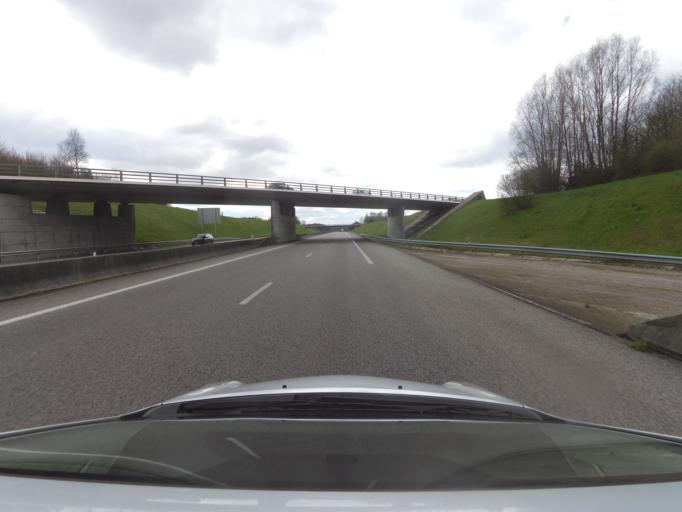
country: FR
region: Haute-Normandie
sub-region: Departement de la Seine-Maritime
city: Saint-Aubin-Routot
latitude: 49.5210
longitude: 0.3032
